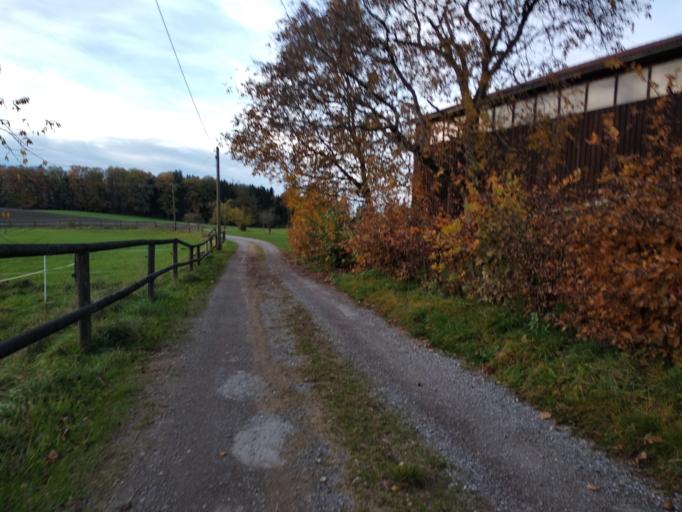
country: DE
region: Bavaria
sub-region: Upper Bavaria
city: Grafing bei Munchen
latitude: 48.0355
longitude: 11.9867
